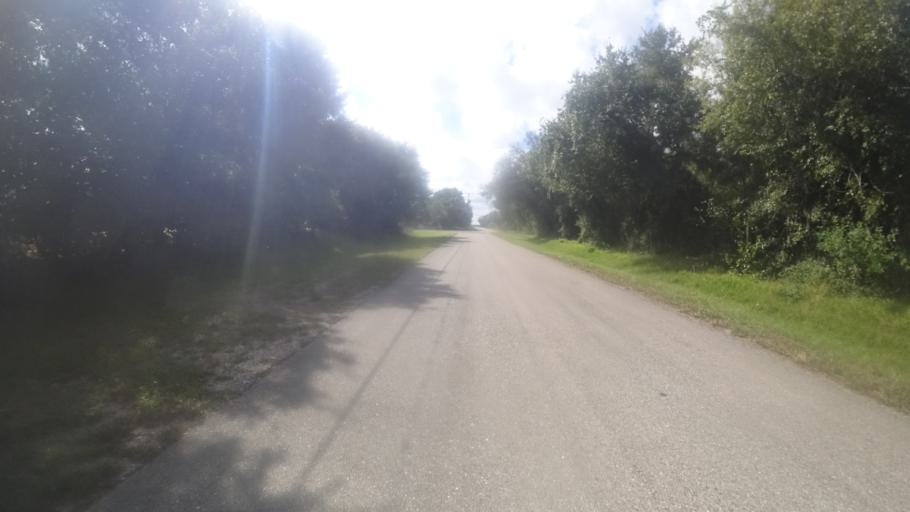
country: US
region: Florida
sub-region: Manatee County
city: Samoset
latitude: 27.4697
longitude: -82.4588
